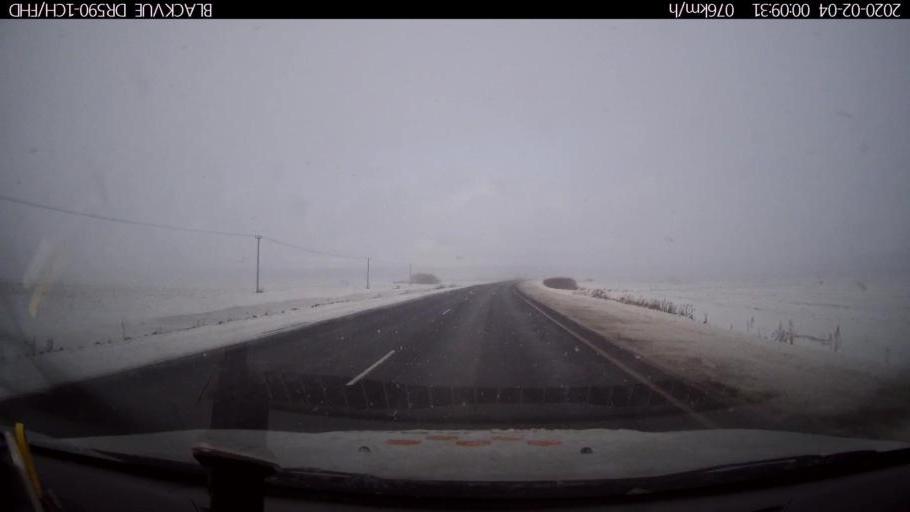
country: RU
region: Nizjnij Novgorod
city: Dal'neye Konstantinovo
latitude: 55.8829
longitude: 44.1383
